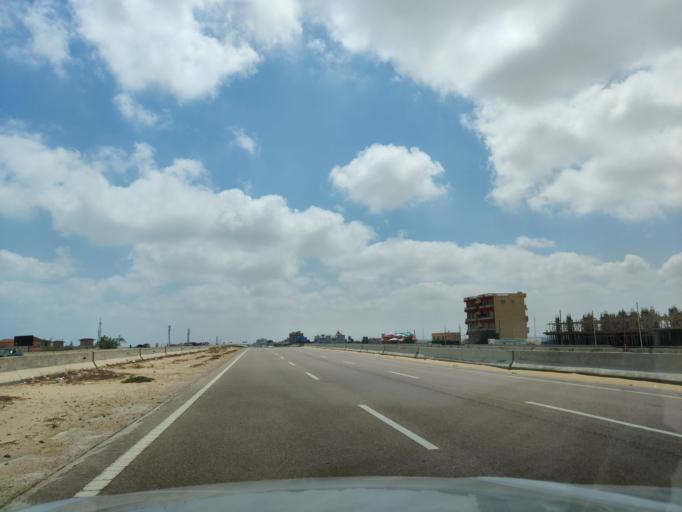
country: EG
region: Muhafazat Matruh
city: Al `Alamayn
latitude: 30.8195
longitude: 29.1616
